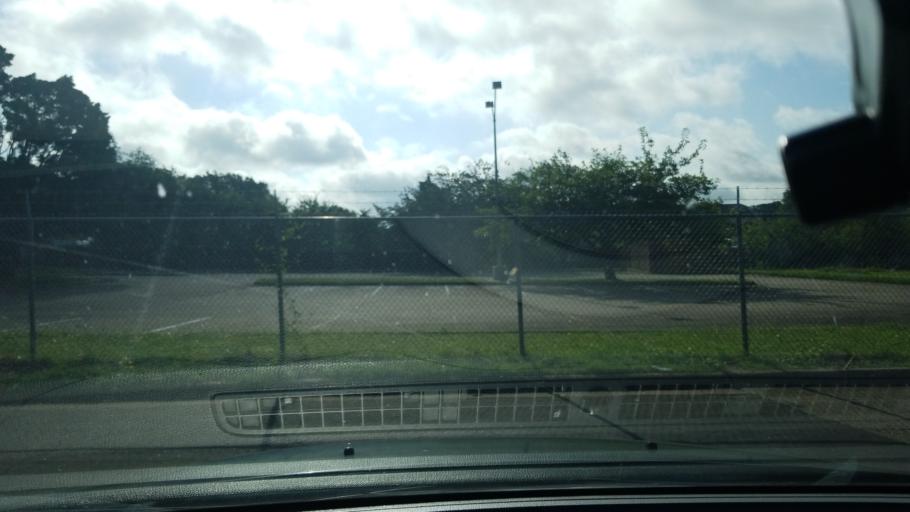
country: US
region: Texas
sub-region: Dallas County
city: Mesquite
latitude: 32.8141
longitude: -96.6823
